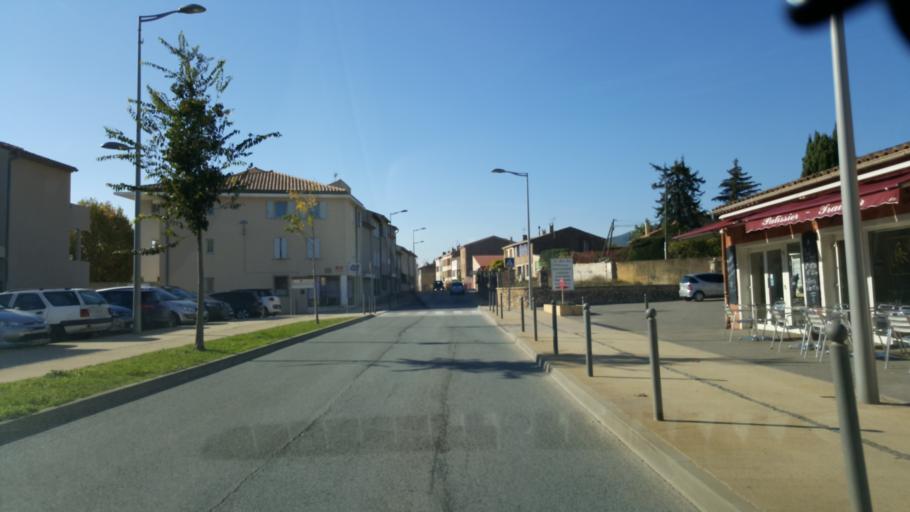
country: FR
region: Provence-Alpes-Cote d'Azur
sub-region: Departement du Var
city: Saint-Zacharie
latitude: 43.3854
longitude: 5.7103
